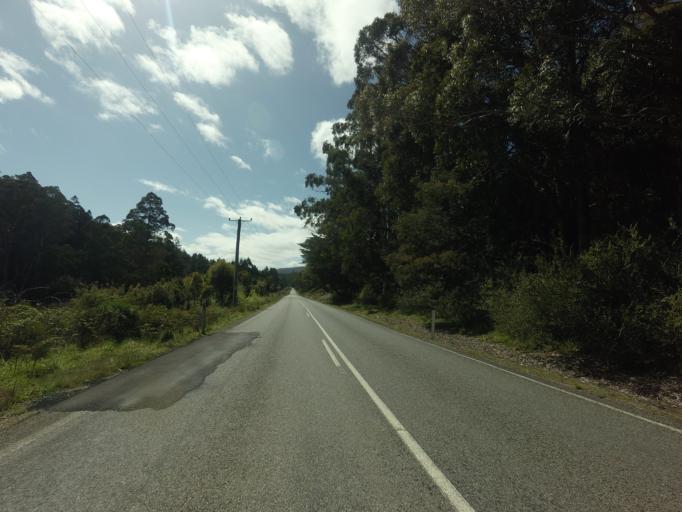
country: AU
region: Tasmania
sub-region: Derwent Valley
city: New Norfolk
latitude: -42.7211
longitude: 146.6810
